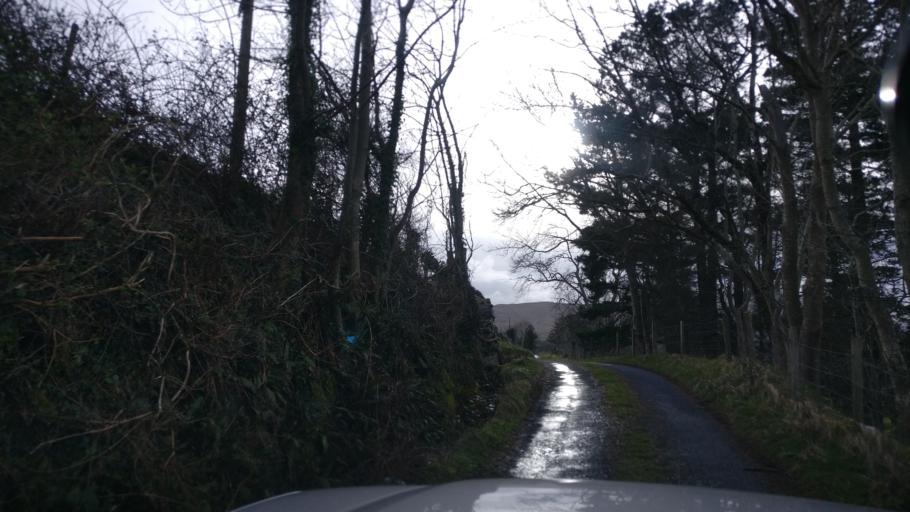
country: IE
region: Connaught
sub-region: County Galway
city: Oughterard
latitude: 53.5595
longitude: -9.4365
